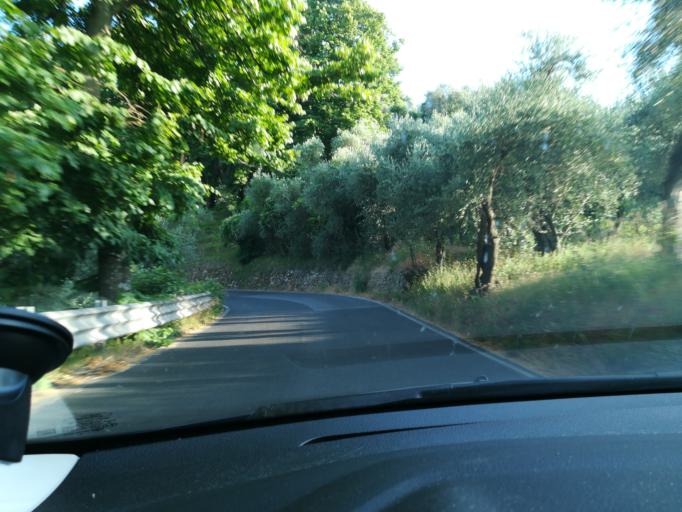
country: IT
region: Tuscany
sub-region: Provincia di Lucca
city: Stiava
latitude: 43.9144
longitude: 10.3402
